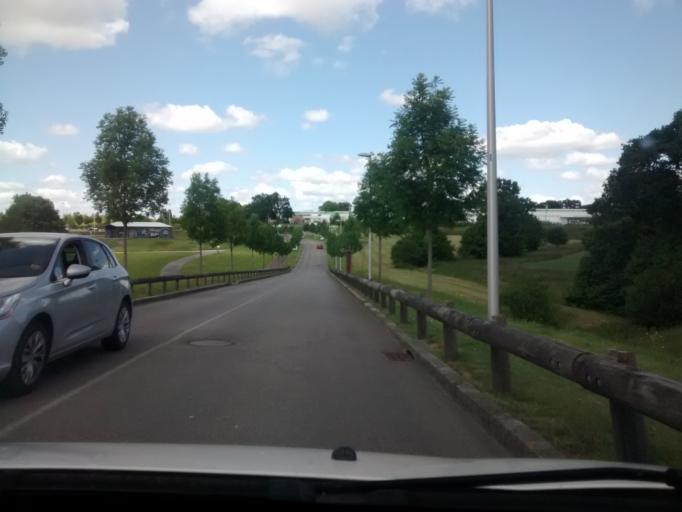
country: FR
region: Brittany
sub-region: Departement d'Ille-et-Vilaine
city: Betton
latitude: 48.1610
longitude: -1.6358
